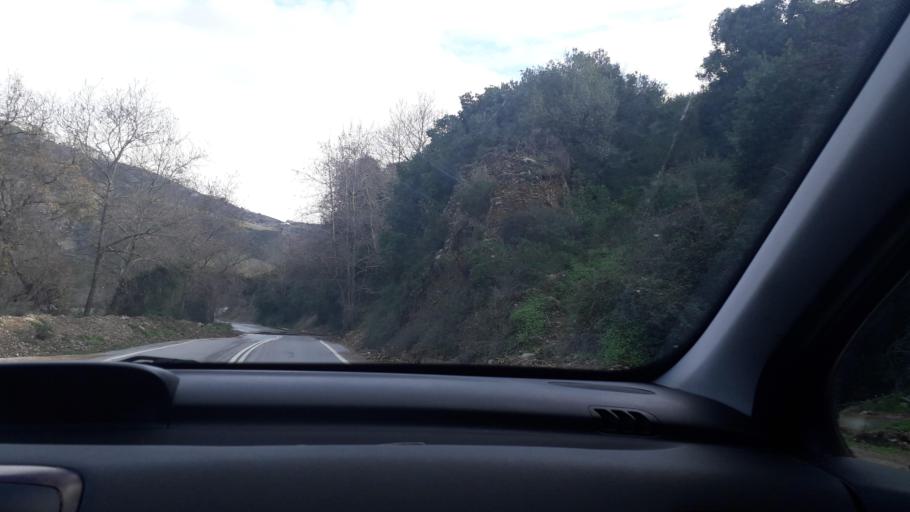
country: GR
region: Crete
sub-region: Nomos Rethymnis
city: Agia Foteini
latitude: 35.2938
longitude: 24.5551
